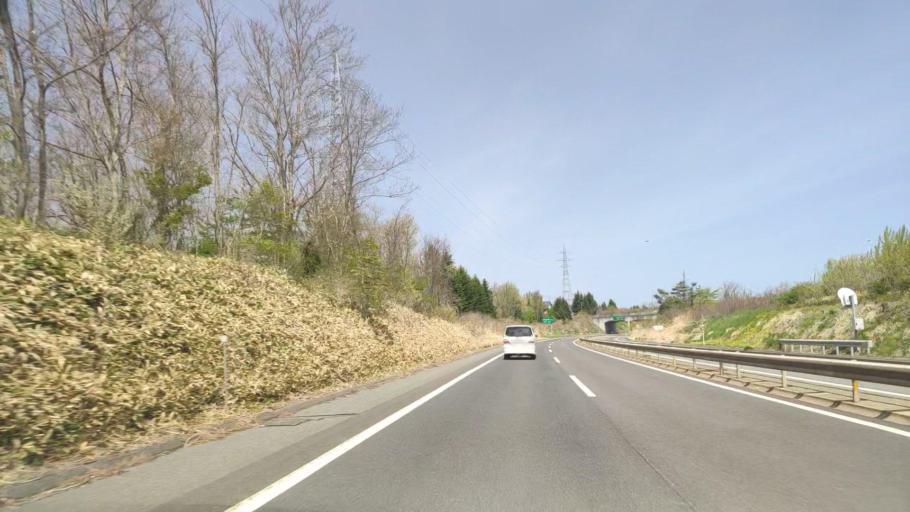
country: JP
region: Aomori
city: Hachinohe
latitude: 40.4753
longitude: 141.4601
